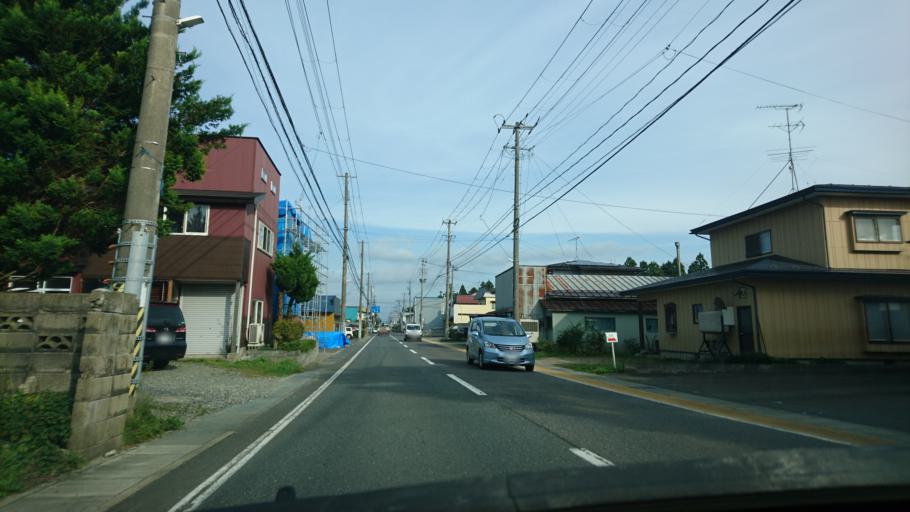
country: JP
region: Iwate
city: Kitakami
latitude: 39.3081
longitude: 140.9925
